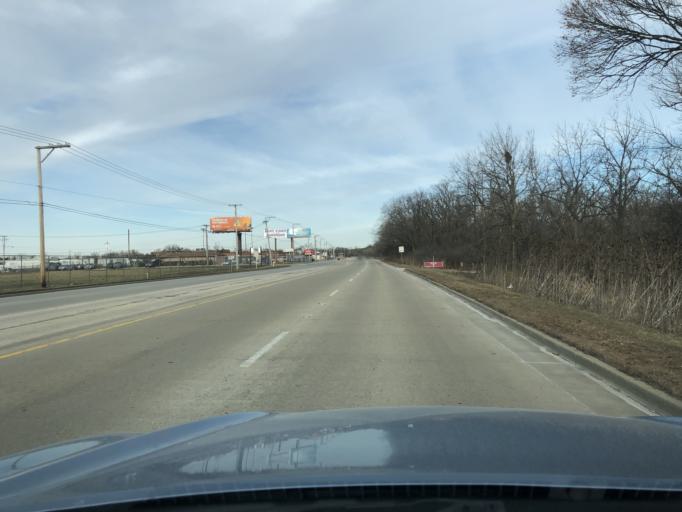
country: US
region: Illinois
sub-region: Cook County
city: Wheeling
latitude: 42.1177
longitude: -87.8947
